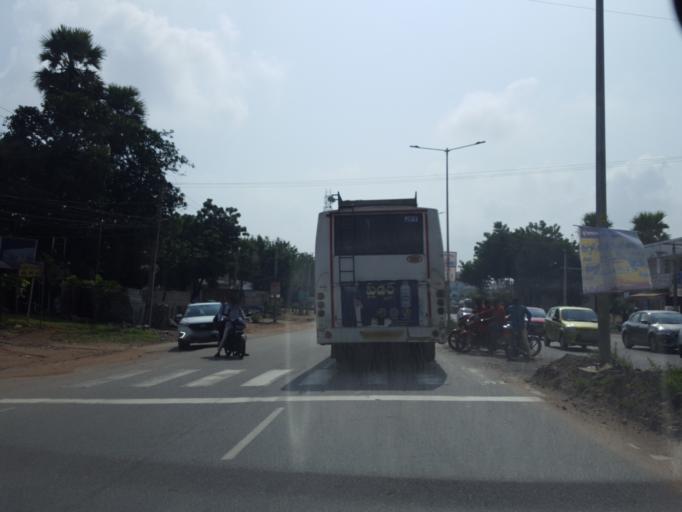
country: IN
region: Telangana
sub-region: Rangareddi
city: Lal Bahadur Nagar
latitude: 17.3111
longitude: 78.6842
